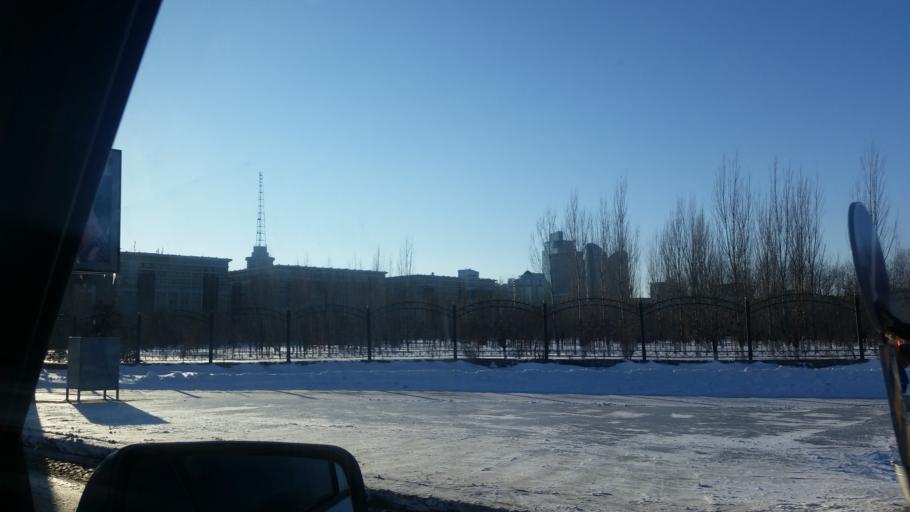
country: KZ
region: Astana Qalasy
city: Astana
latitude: 51.1350
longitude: 71.4414
